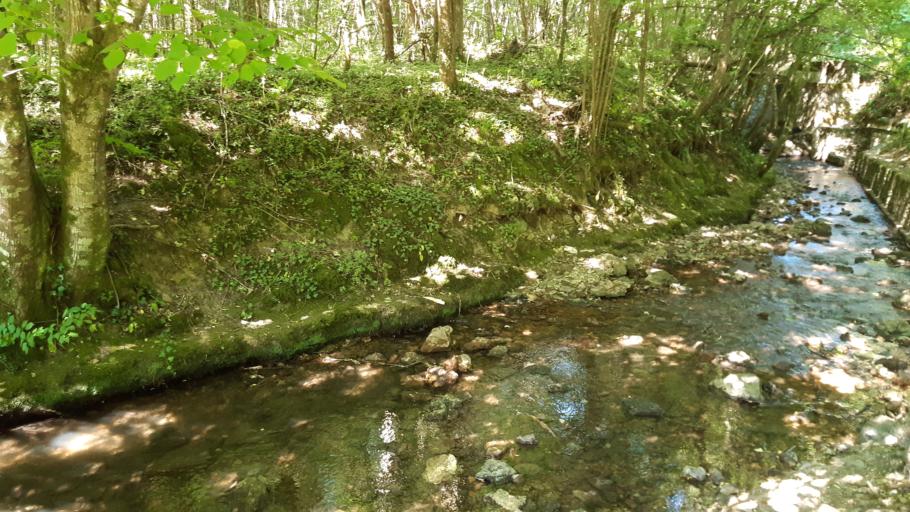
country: FR
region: Centre
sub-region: Departement d'Indre-et-Loire
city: Mettray
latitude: 47.4375
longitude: 0.6579
